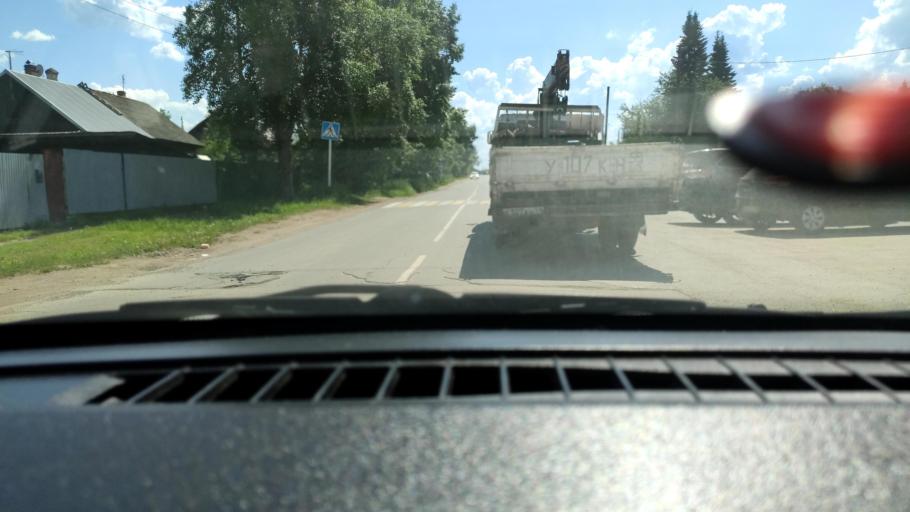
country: RU
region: Perm
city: Sylva
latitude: 58.0327
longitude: 56.7594
